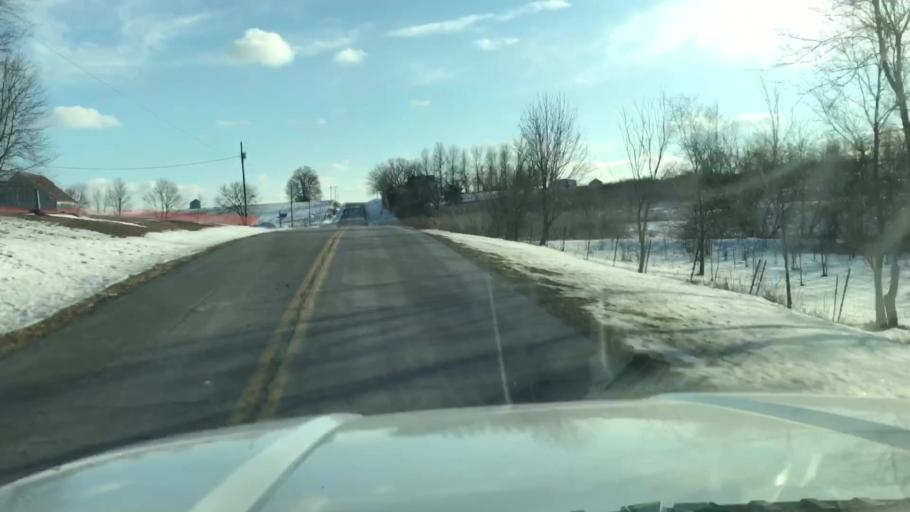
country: US
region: Missouri
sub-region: Holt County
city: Oregon
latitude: 40.0591
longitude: -94.9749
